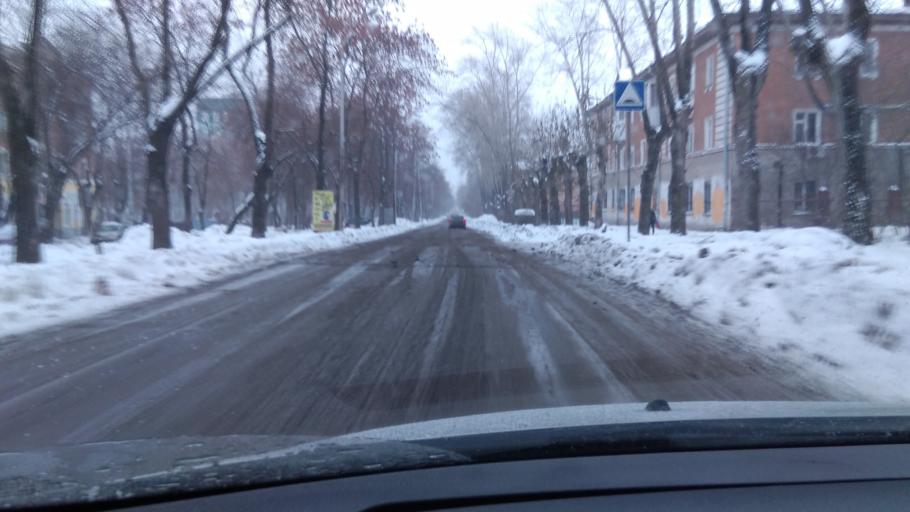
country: RU
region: Sverdlovsk
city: Yekaterinburg
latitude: 56.8968
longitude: 60.5806
